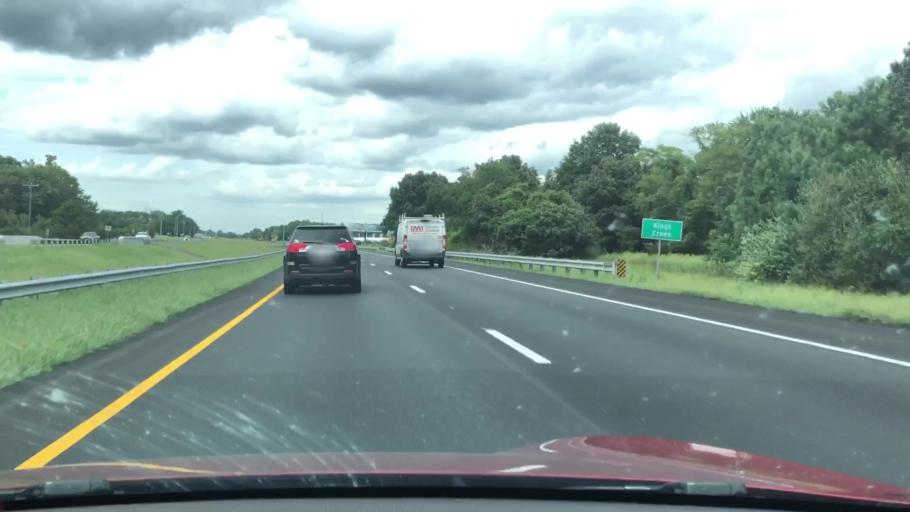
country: US
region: Maryland
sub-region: Somerset County
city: Princess Anne
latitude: 38.1645
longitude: -75.6890
